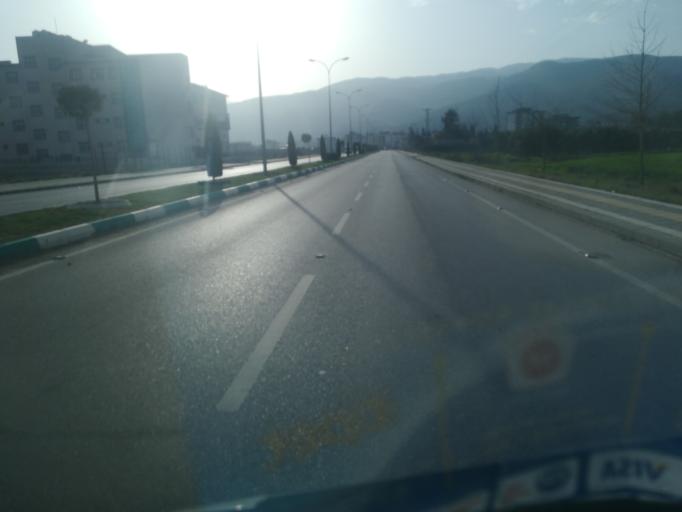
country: TR
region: Osmaniye
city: Osmaniye
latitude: 37.0522
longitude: 36.2246
